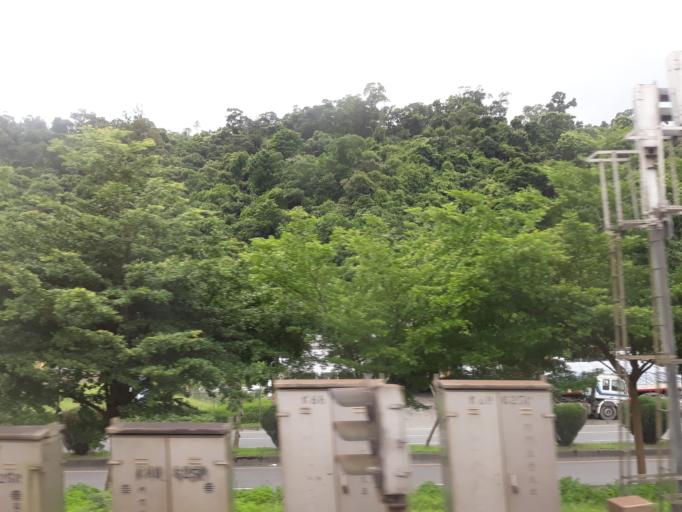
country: TW
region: Taiwan
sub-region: Yilan
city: Yilan
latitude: 24.6152
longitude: 121.8162
